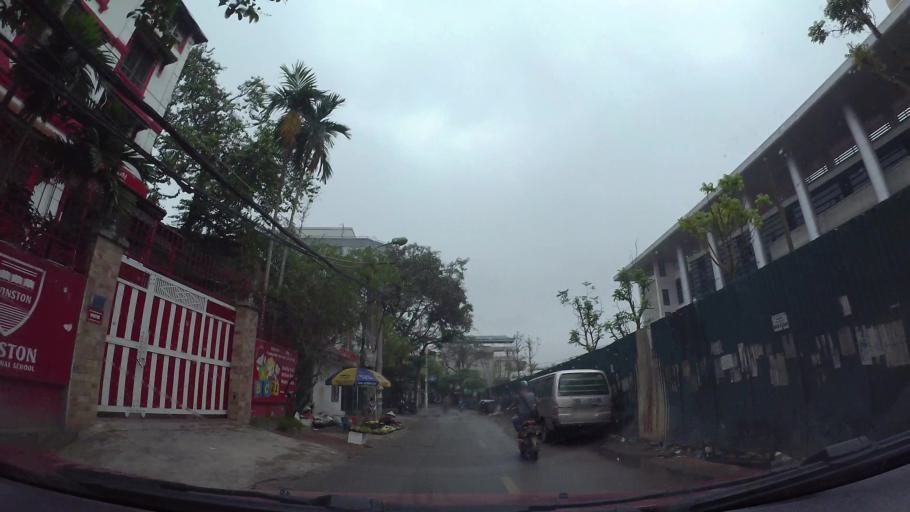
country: VN
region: Ha Noi
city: Dong Da
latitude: 21.0140
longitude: 105.8222
